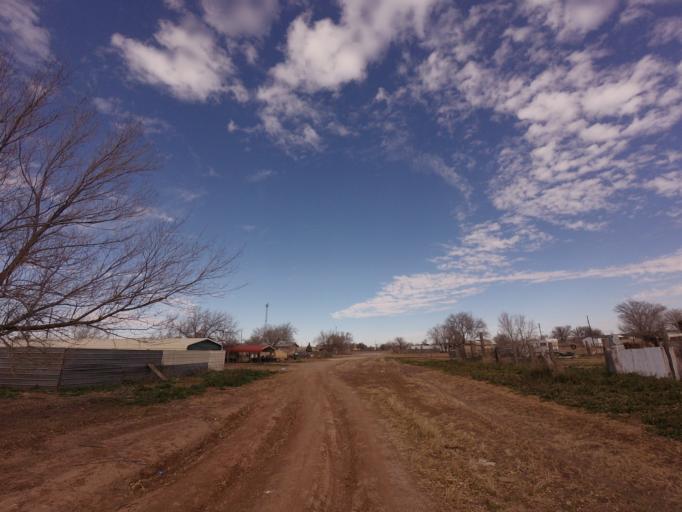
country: US
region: New Mexico
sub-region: Curry County
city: Clovis
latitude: 34.3967
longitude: -103.2292
